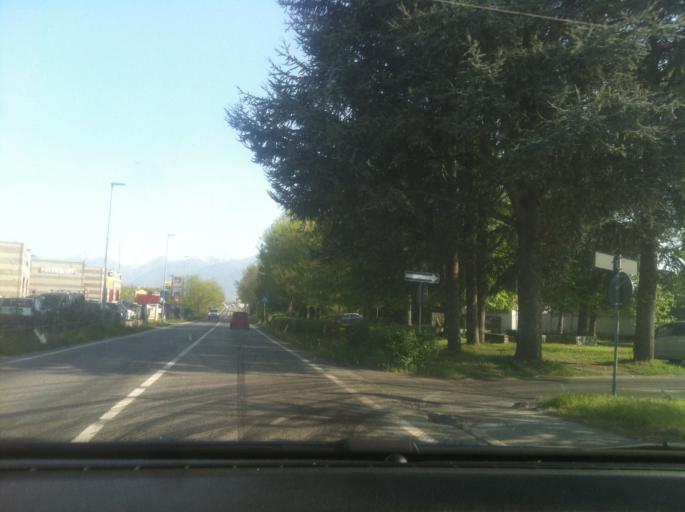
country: IT
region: Piedmont
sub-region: Provincia di Torino
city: Strambino
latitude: 45.3887
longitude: 7.8850
